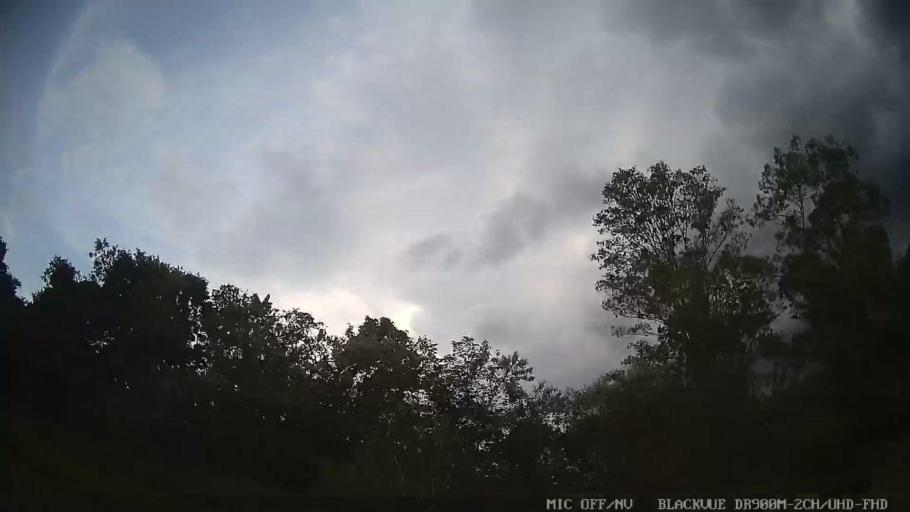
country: BR
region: Sao Paulo
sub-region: Itatiba
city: Itatiba
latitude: -22.9488
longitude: -46.8162
